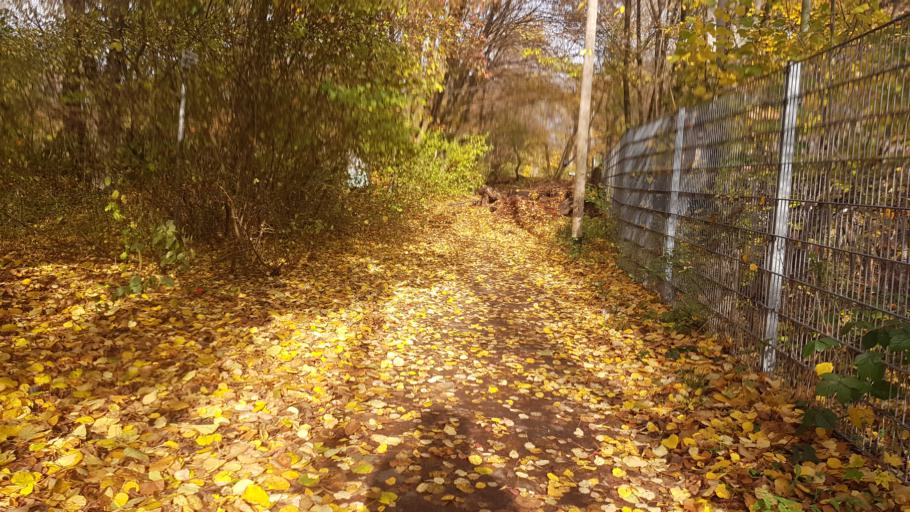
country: DE
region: Bavaria
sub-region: Upper Bavaria
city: Unterhaching
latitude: 48.1040
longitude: 11.6107
